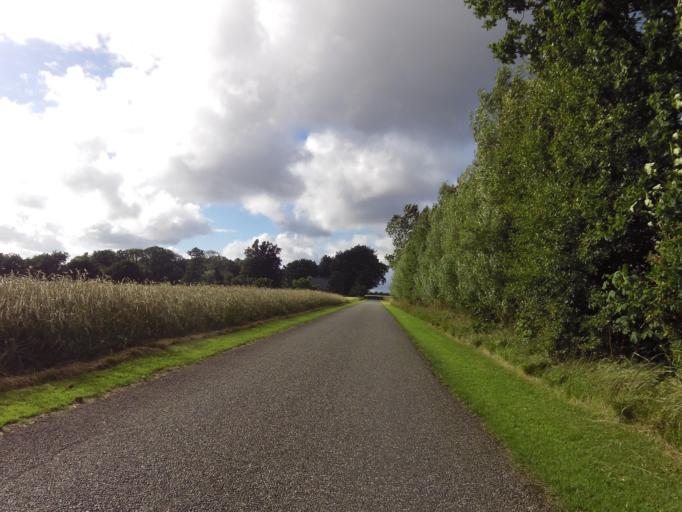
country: DK
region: South Denmark
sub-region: Tonder Kommune
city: Toftlund
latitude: 55.1293
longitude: 9.0776
